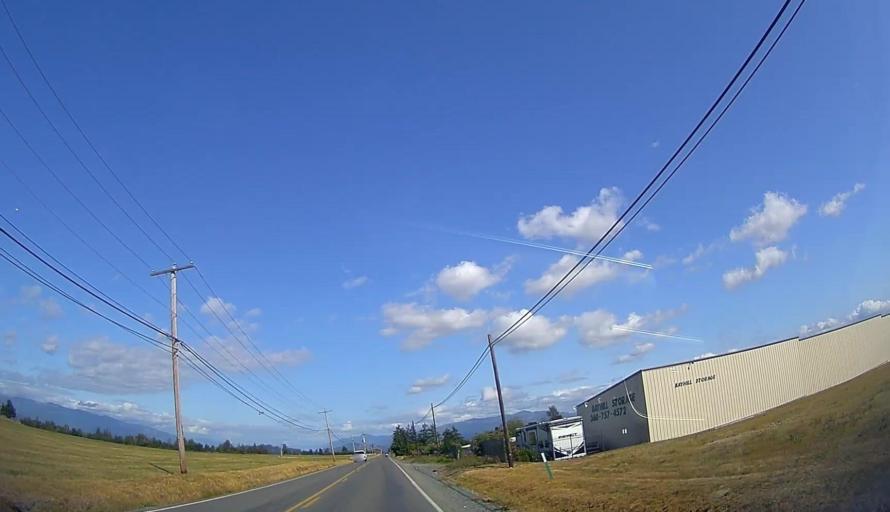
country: US
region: Washington
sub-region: Skagit County
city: Burlington
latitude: 48.4722
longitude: -122.4022
